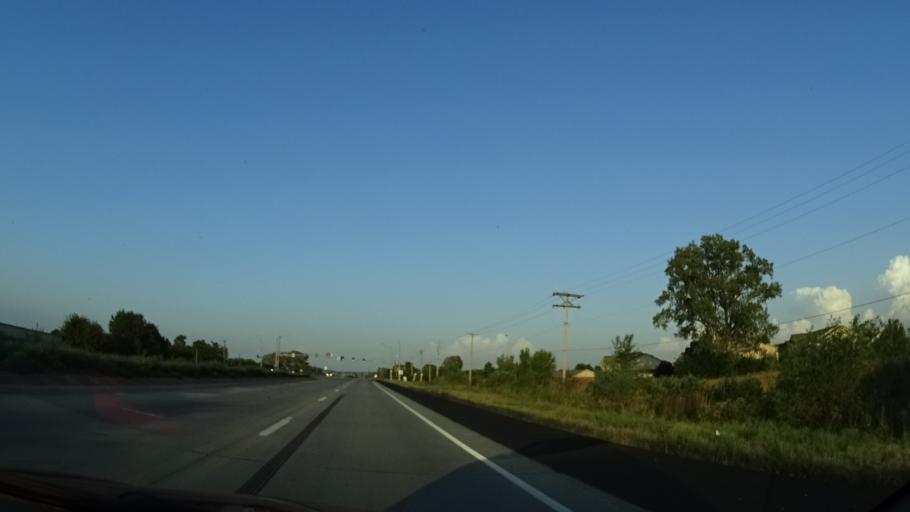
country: US
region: Iowa
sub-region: Pottawattamie County
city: Council Bluffs
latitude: 41.2140
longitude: -95.8917
